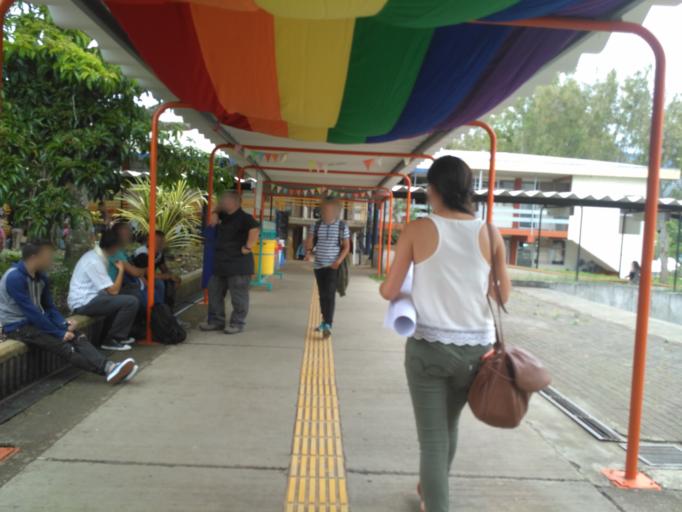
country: CR
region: Cartago
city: Cartago
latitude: 9.8556
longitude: -83.9126
